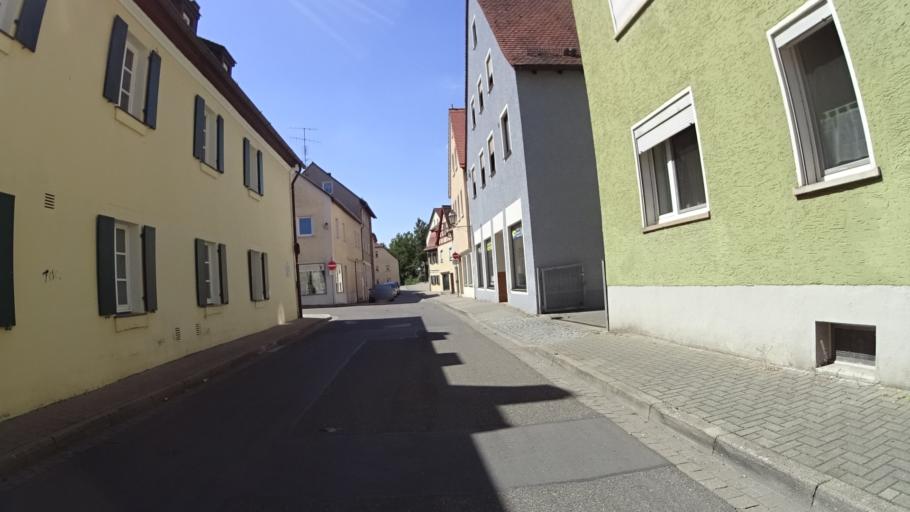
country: DE
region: Bavaria
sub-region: Regierungsbezirk Mittelfranken
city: Gunzenhausen
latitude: 49.1164
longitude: 10.7527
